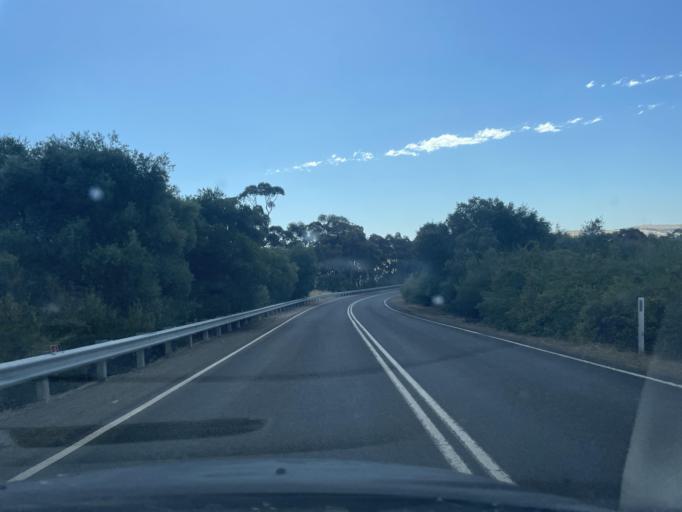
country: AU
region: South Australia
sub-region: Clare and Gilbert Valleys
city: Clare
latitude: -33.9045
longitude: 138.6957
